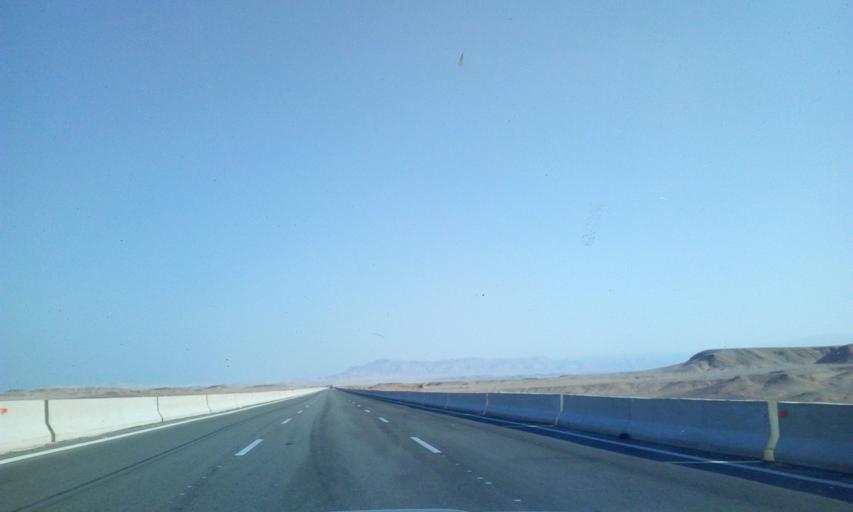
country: EG
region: As Suways
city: Ain Sukhna
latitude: 29.1575
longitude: 32.5126
